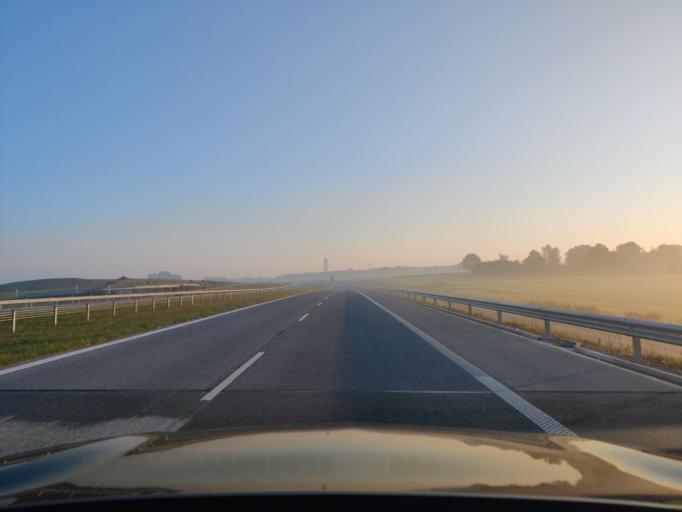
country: PL
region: Masovian Voivodeship
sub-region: Powiat mlawski
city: Mlawa
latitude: 53.0833
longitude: 20.3969
